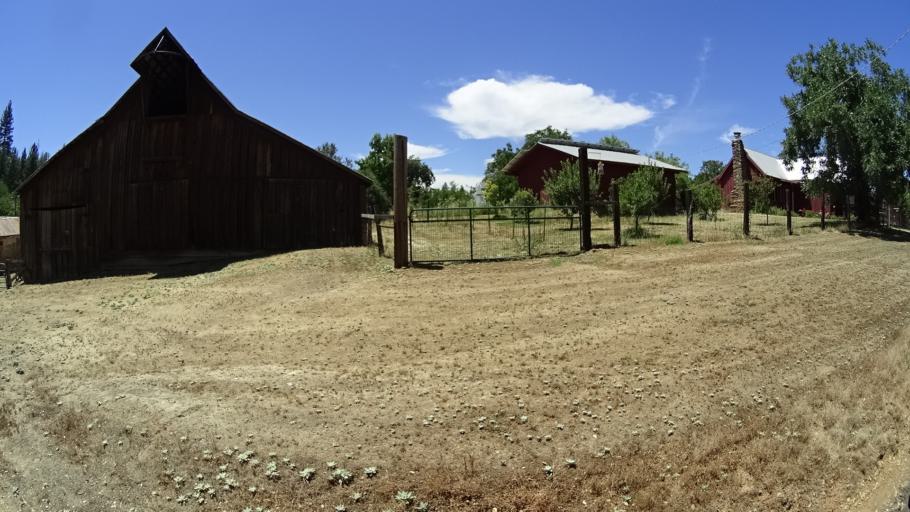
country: US
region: California
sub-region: Calaveras County
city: Forest Meadows
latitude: 38.2095
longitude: -120.4651
